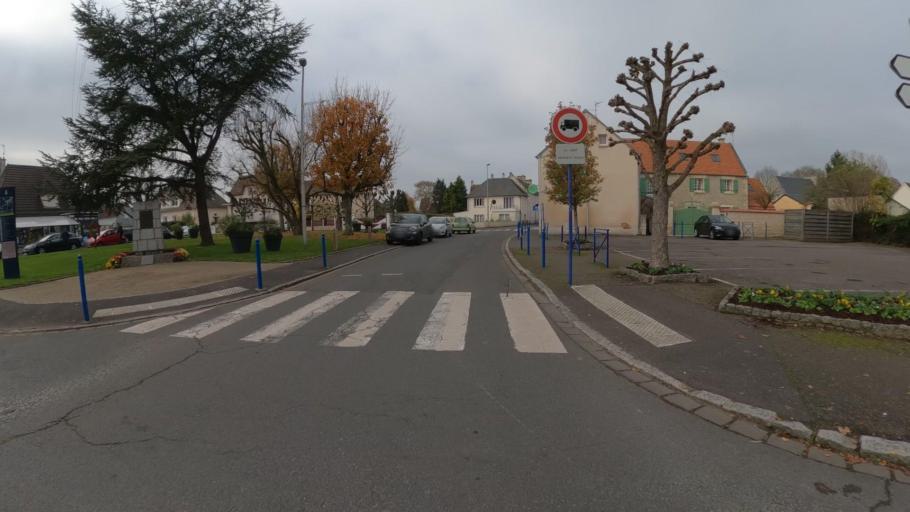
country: FR
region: Lower Normandy
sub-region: Departement du Calvados
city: Authie
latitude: 49.2066
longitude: -0.4313
